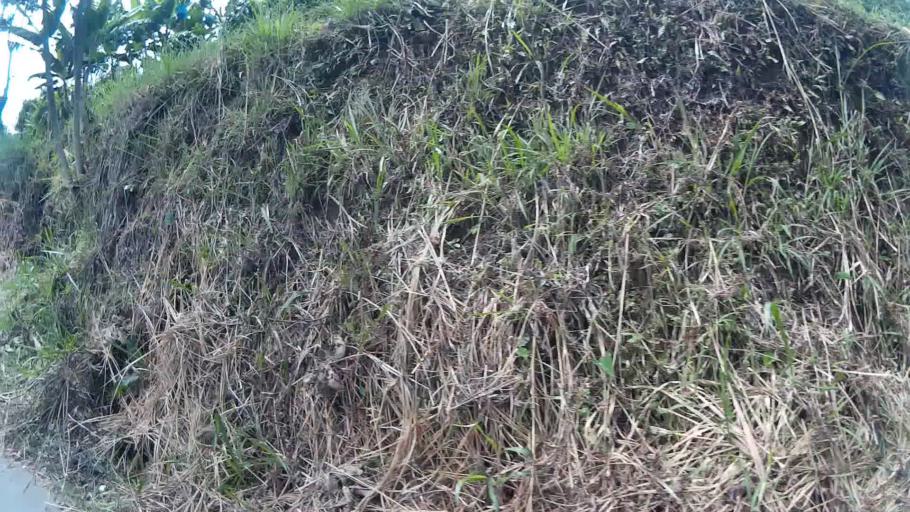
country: CO
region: Risaralda
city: Marsella
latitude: 4.8792
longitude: -75.7599
